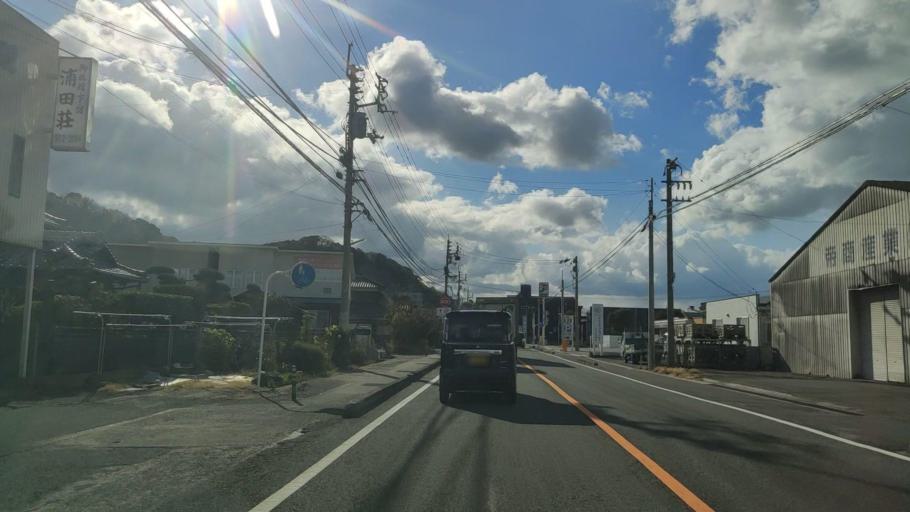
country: JP
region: Ehime
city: Masaki-cho
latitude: 33.8367
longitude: 132.7092
